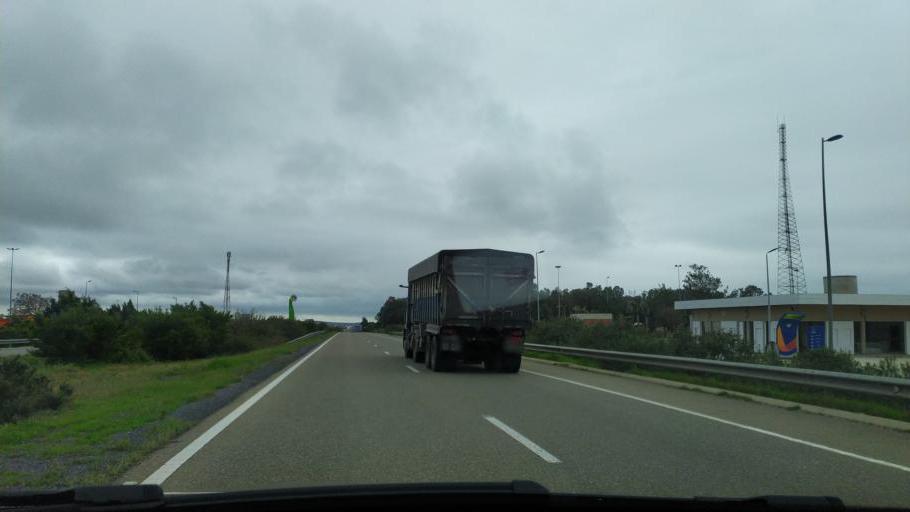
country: MA
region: Gharb-Chrarda-Beni Hssen
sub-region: Kenitra Province
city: Lalla Mimouna
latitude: 34.8771
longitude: -6.2136
